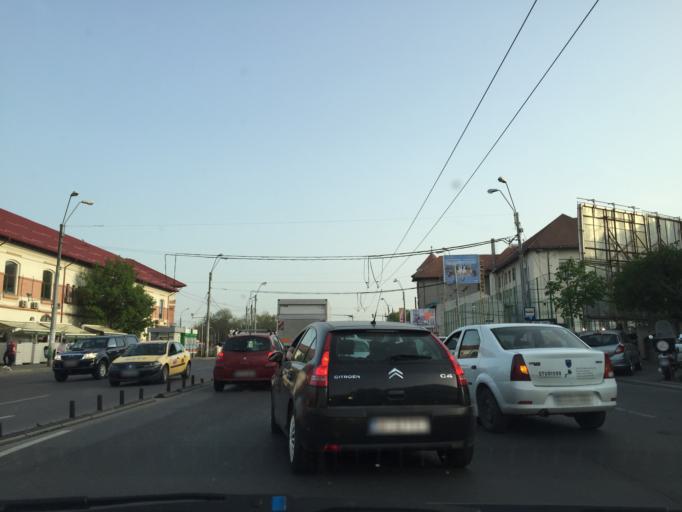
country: RO
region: Bucuresti
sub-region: Municipiul Bucuresti
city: Bucuresti
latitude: 44.4155
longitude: 26.1044
